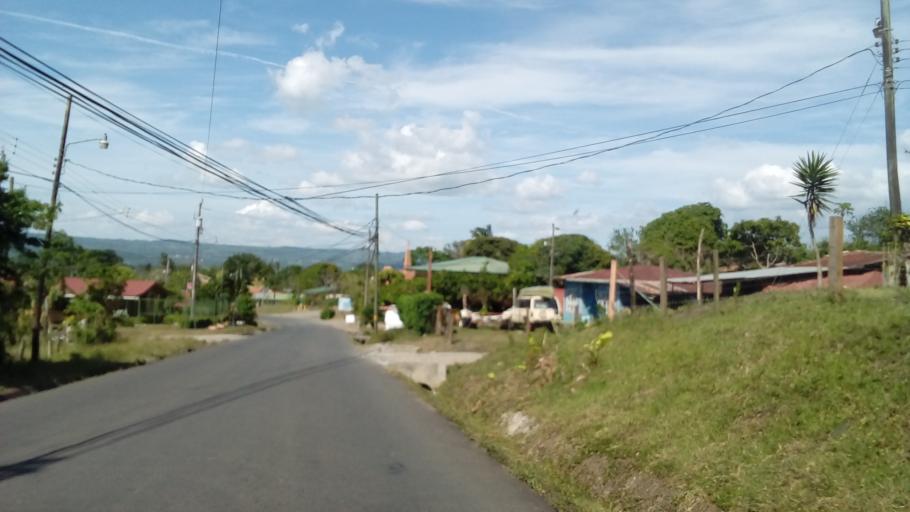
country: CR
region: Guanacaste
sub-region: Canton de Tilaran
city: Tilaran
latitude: 10.5010
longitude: -84.9444
